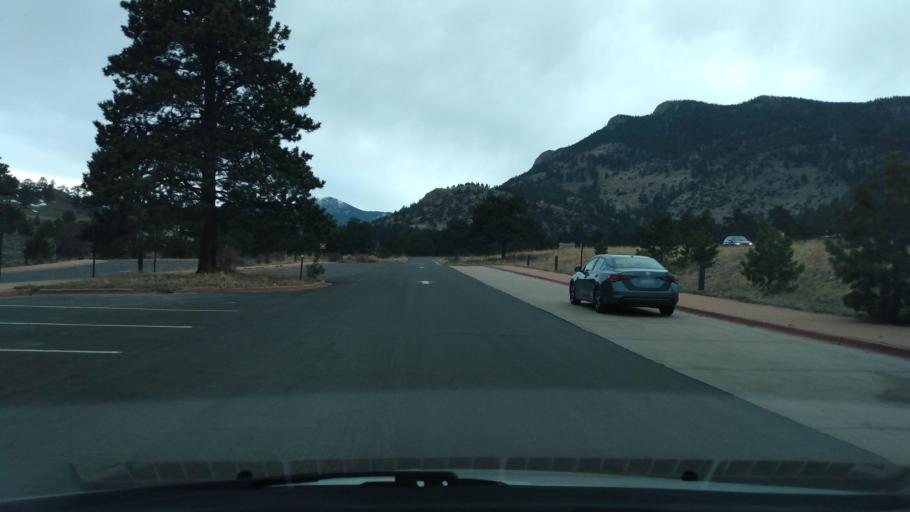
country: US
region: Colorado
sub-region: Larimer County
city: Estes Park
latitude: 40.3666
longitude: -105.5611
